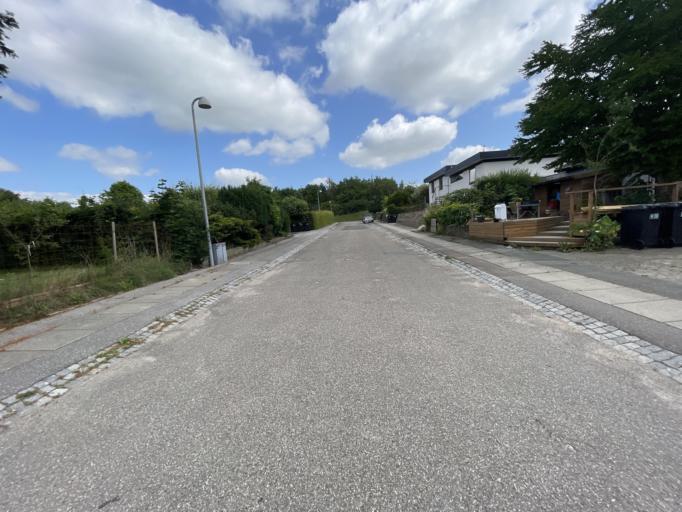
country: DK
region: Zealand
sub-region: Roskilde Kommune
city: Gundsomagle
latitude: 55.7406
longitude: 12.1546
